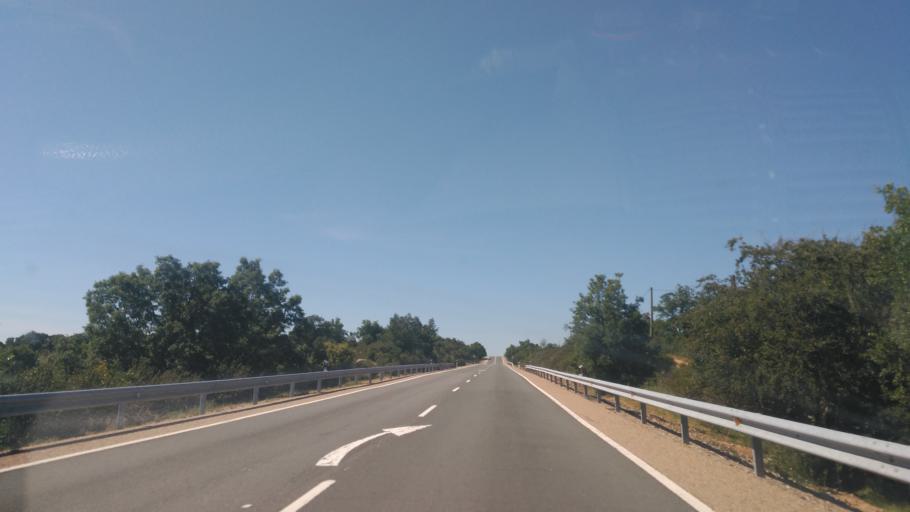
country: ES
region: Castille and Leon
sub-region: Provincia de Zamora
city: Cuelgamures
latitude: 41.2743
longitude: -5.7166
